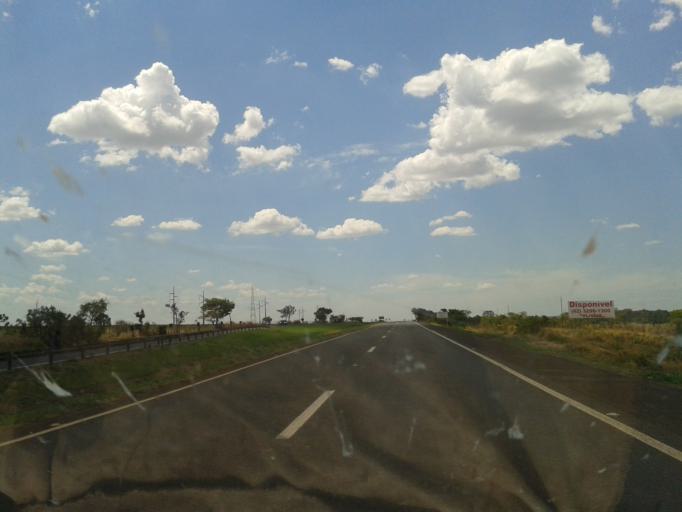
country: BR
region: Minas Gerais
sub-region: Uberlandia
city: Uberlandia
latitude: -19.0531
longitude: -48.1955
